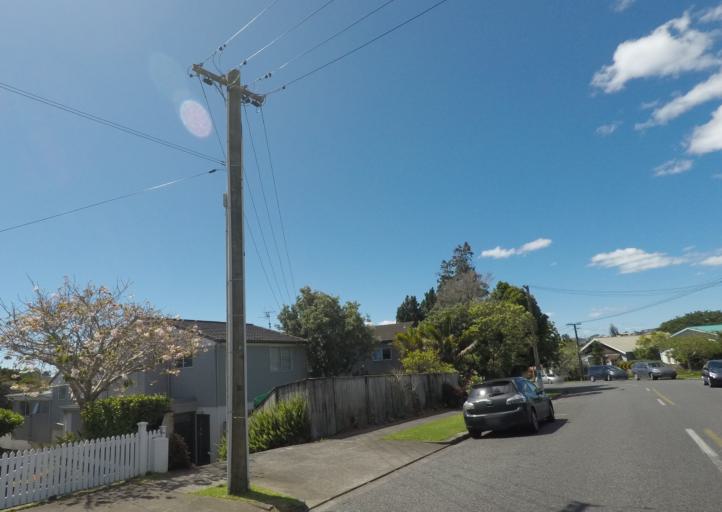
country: NZ
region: Auckland
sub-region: Auckland
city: Auckland
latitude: -36.8713
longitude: 174.7335
